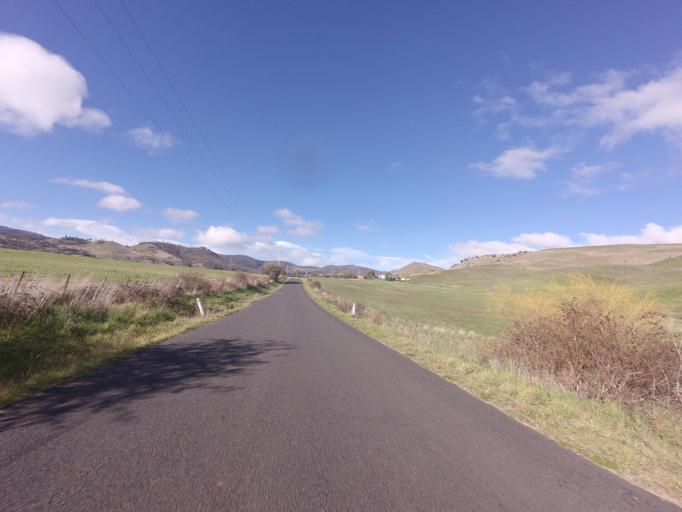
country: AU
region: Tasmania
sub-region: Derwent Valley
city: New Norfolk
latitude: -42.6947
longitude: 146.9585
